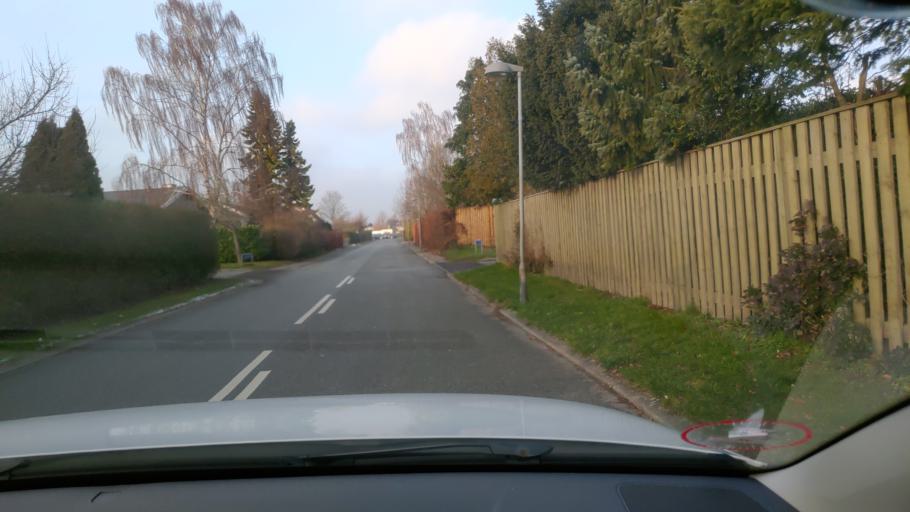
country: DK
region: Zealand
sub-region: Solrod Kommune
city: Solrod Strand
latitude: 55.5415
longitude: 12.2213
